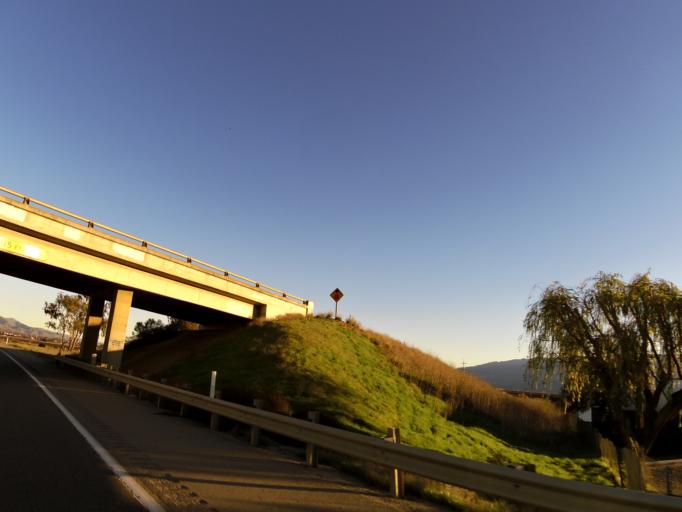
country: US
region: California
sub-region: Monterey County
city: Gonzales
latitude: 36.5235
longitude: -121.4646
